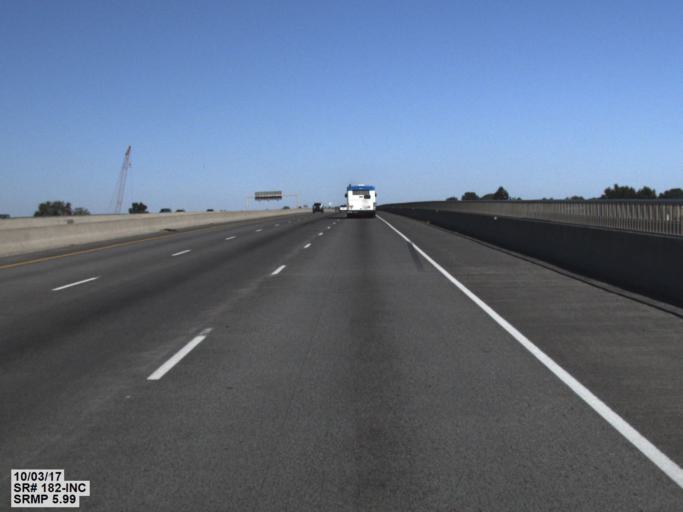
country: US
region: Washington
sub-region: Benton County
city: Richland
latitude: 46.2639
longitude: -119.2435
